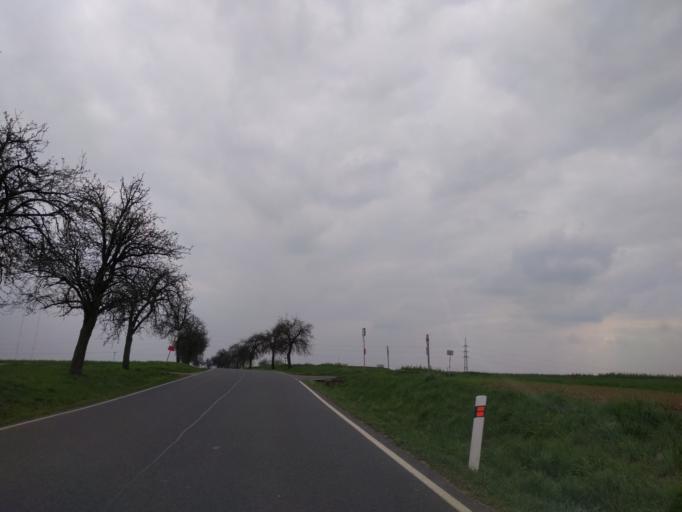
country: CZ
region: Central Bohemia
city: Cesky Brod
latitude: 50.0914
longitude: 14.8647
